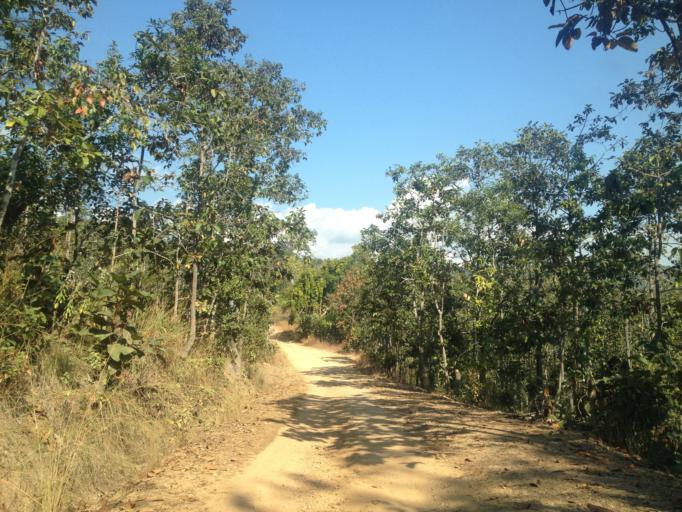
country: TH
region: Mae Hong Son
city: Ban Huai I Huak
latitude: 18.1258
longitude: 98.1974
